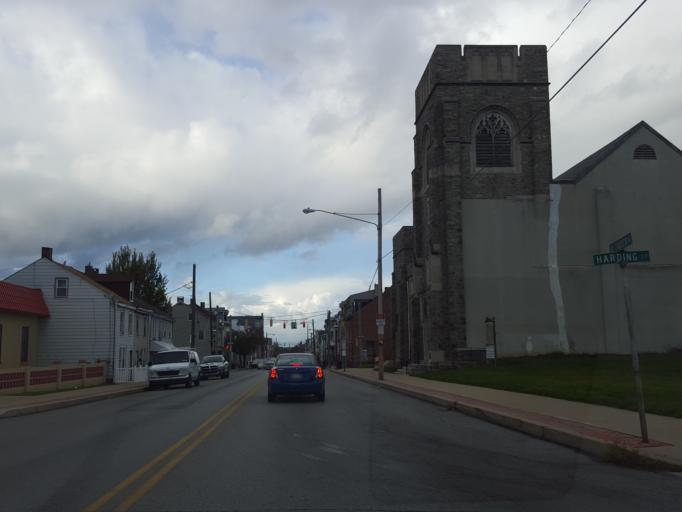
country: US
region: Pennsylvania
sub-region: York County
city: York
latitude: 39.9573
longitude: -76.7206
